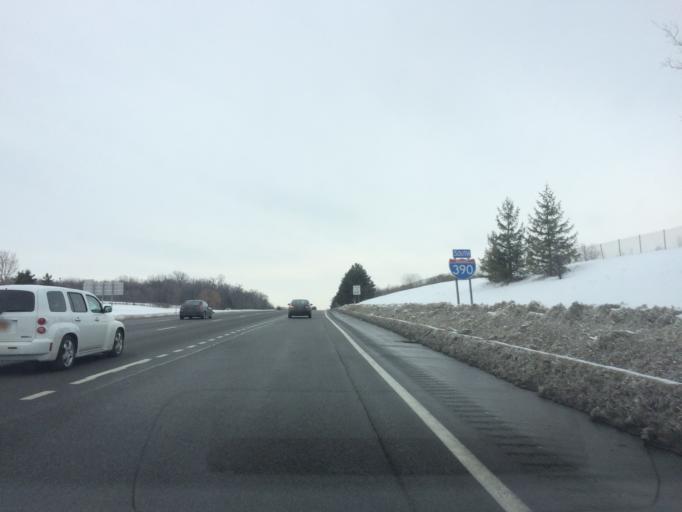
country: US
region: New York
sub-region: Monroe County
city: Rochester
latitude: 43.0830
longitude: -77.6112
